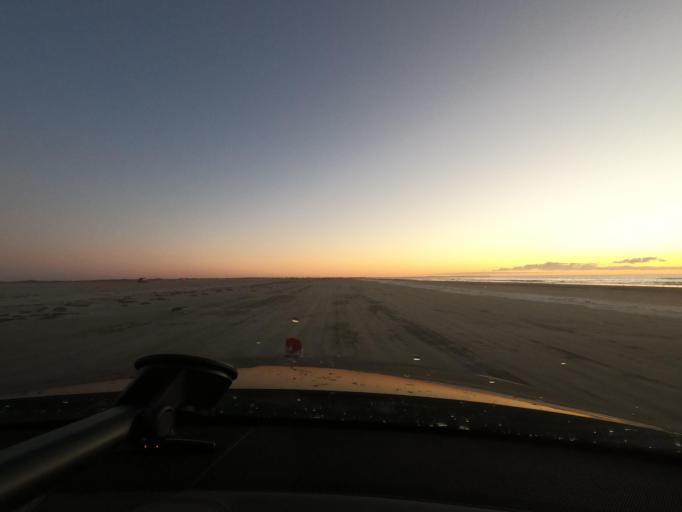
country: DE
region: Schleswig-Holstein
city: List
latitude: 55.1573
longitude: 8.4774
